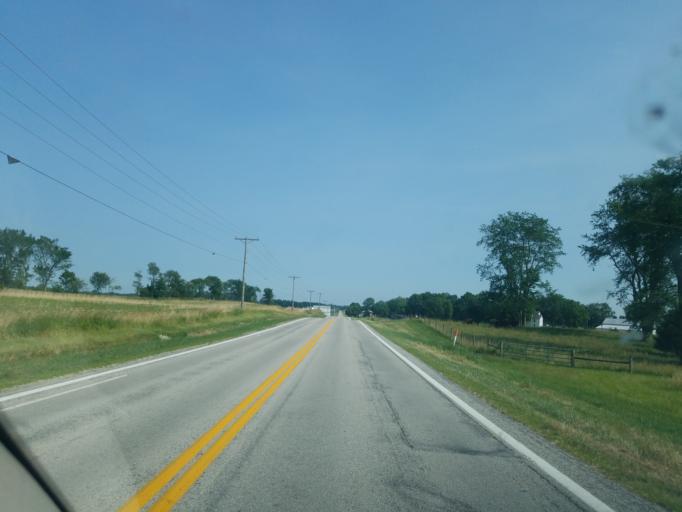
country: US
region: Ohio
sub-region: Wyandot County
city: Carey
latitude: 41.0120
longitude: -83.2833
